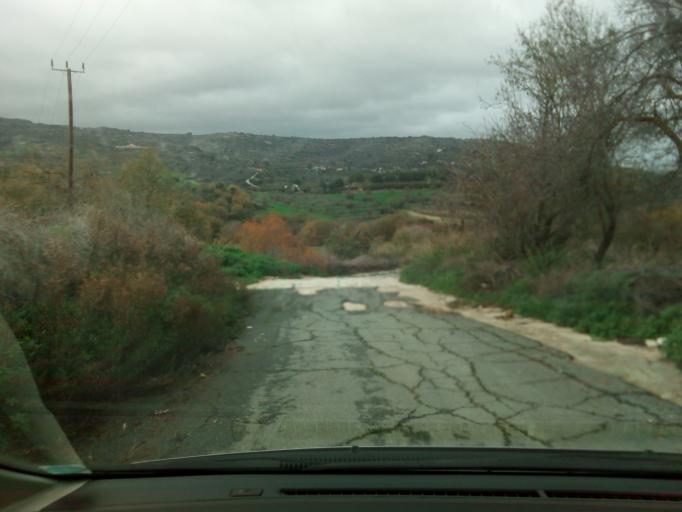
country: CY
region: Pafos
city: Tala
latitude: 34.9295
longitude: 32.4711
